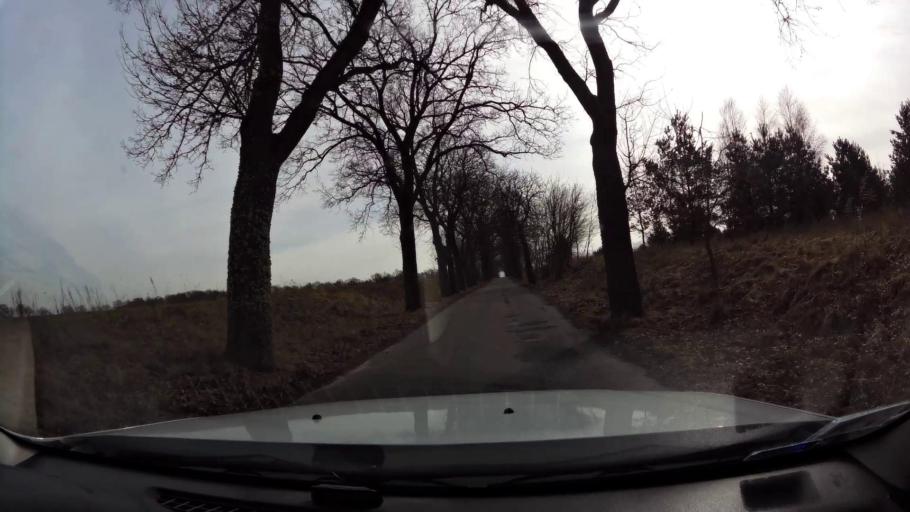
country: PL
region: West Pomeranian Voivodeship
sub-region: Powiat stargardzki
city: Insko
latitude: 53.4495
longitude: 15.6391
